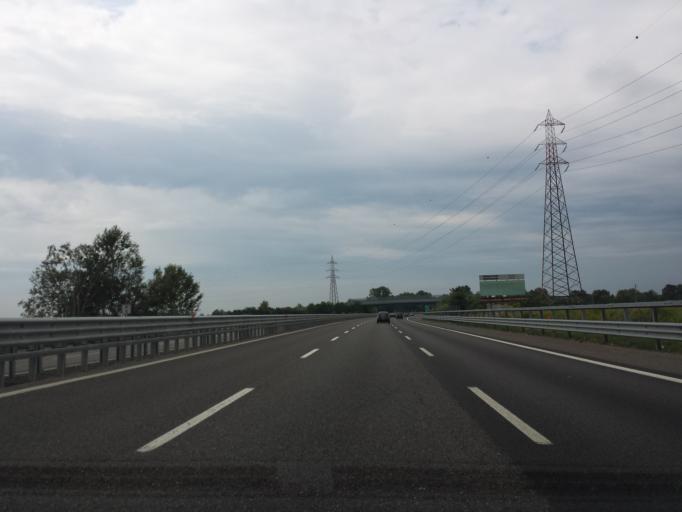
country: IT
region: Lombardy
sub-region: Citta metropolitana di Milano
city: Zibido San Giacomo
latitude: 45.3770
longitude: 9.1314
